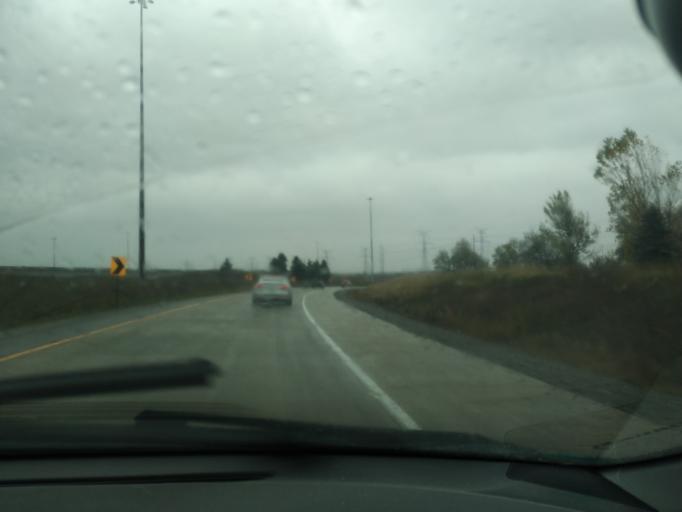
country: CA
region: Ontario
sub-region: York
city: Richmond Hill
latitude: 43.8377
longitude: -79.3719
